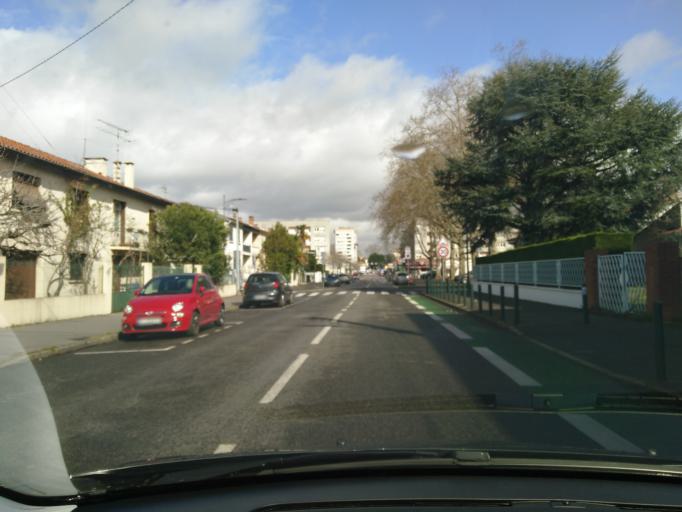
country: FR
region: Midi-Pyrenees
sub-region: Departement de la Haute-Garonne
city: Toulouse
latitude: 43.5787
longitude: 1.4583
